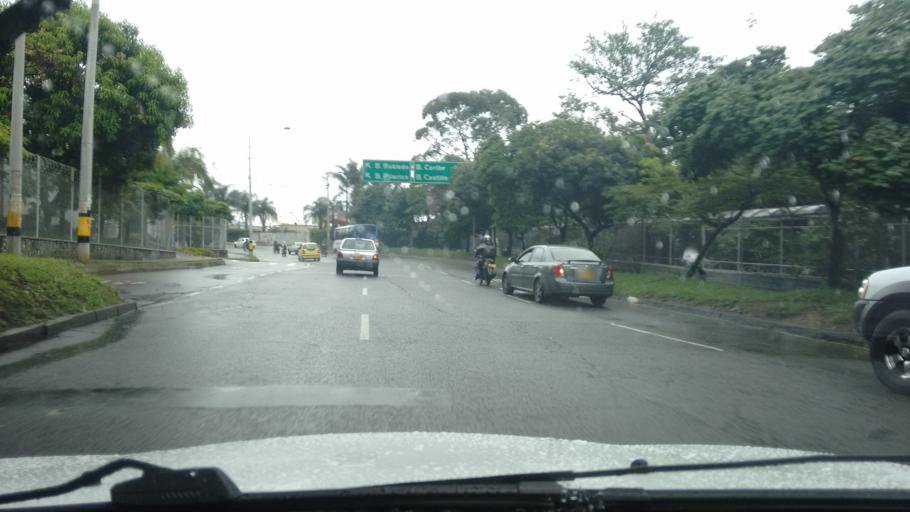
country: CO
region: Antioquia
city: Medellin
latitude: 6.2679
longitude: -75.5761
